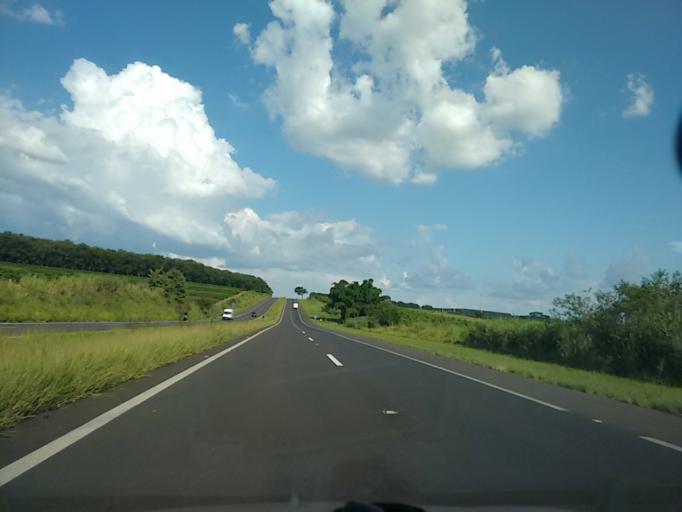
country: BR
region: Sao Paulo
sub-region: Duartina
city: Duartina
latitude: -22.3269
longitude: -49.4727
